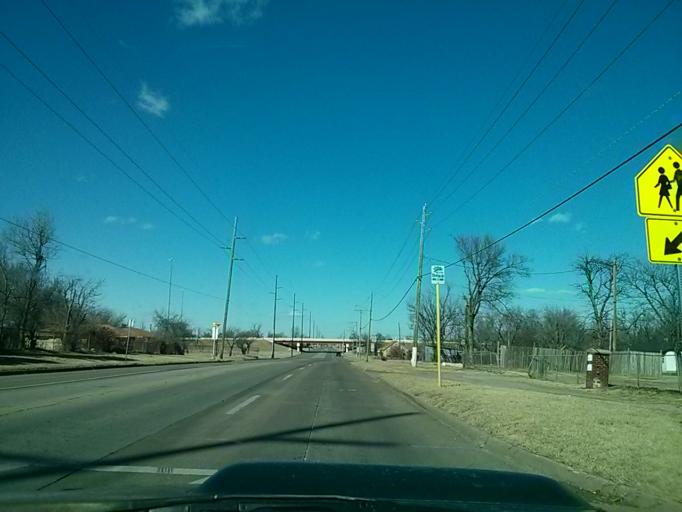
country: US
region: Oklahoma
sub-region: Tulsa County
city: Turley
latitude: 36.1952
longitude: -95.9581
